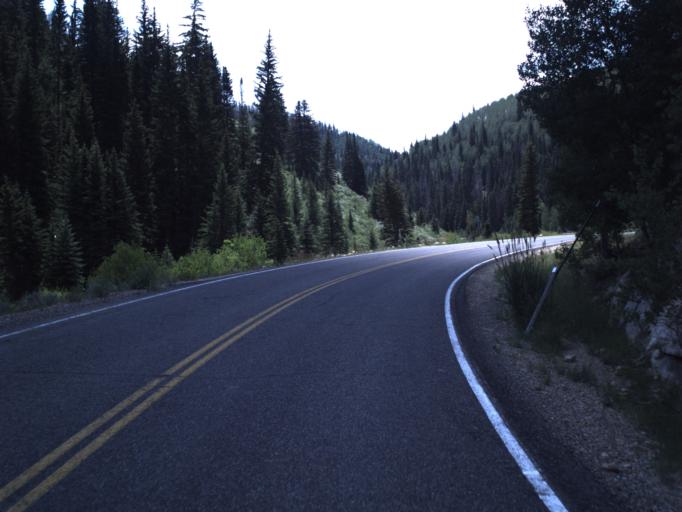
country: US
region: Utah
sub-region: Sanpete County
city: Fairview
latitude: 39.6733
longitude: -111.1550
